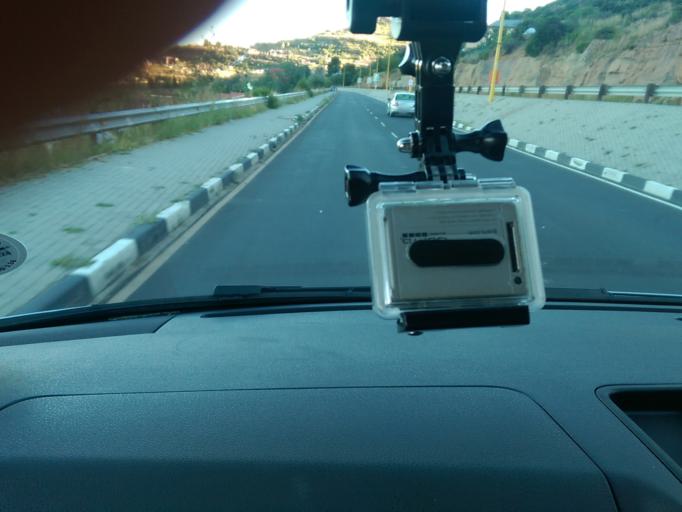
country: LS
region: Maseru
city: Maseru
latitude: -29.3205
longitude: 27.4948
